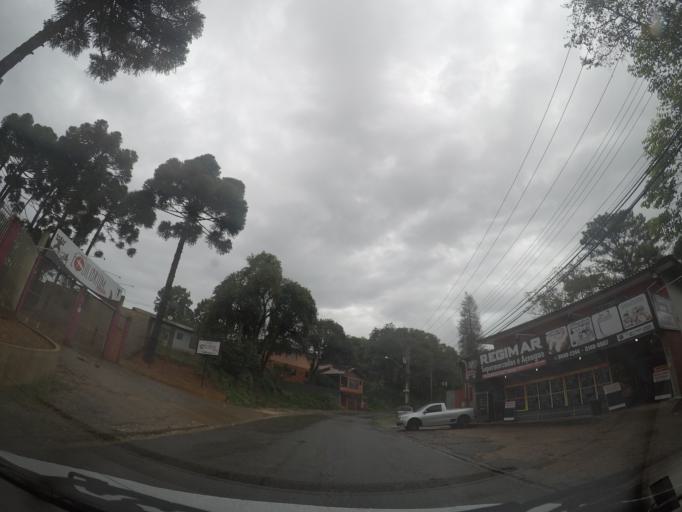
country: BR
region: Parana
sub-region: Curitiba
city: Curitiba
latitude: -25.4615
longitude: -49.3918
